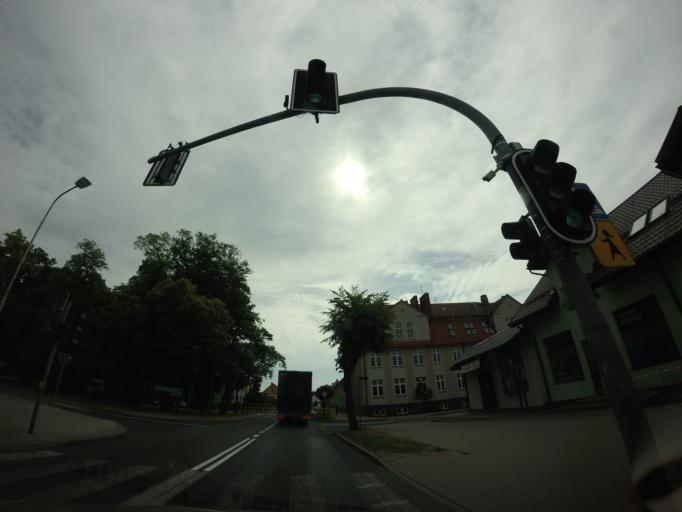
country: PL
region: West Pomeranian Voivodeship
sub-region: Powiat walecki
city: Miroslawiec
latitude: 53.3425
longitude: 16.0892
